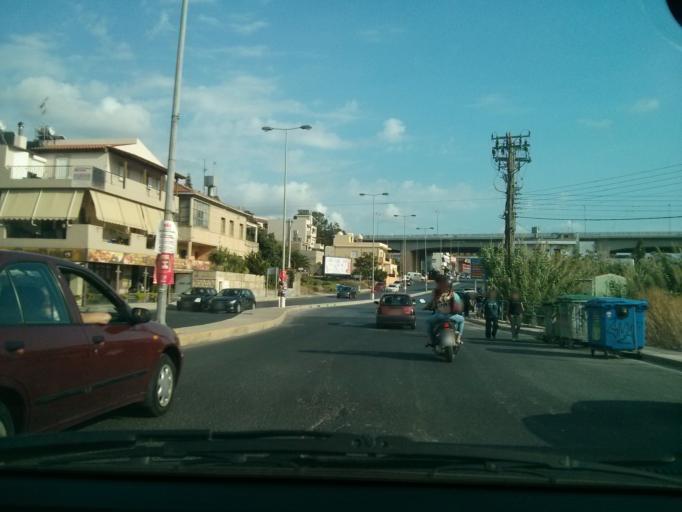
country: GR
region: Crete
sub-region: Nomos Irakleiou
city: Irakleion
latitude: 35.3222
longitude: 25.1423
